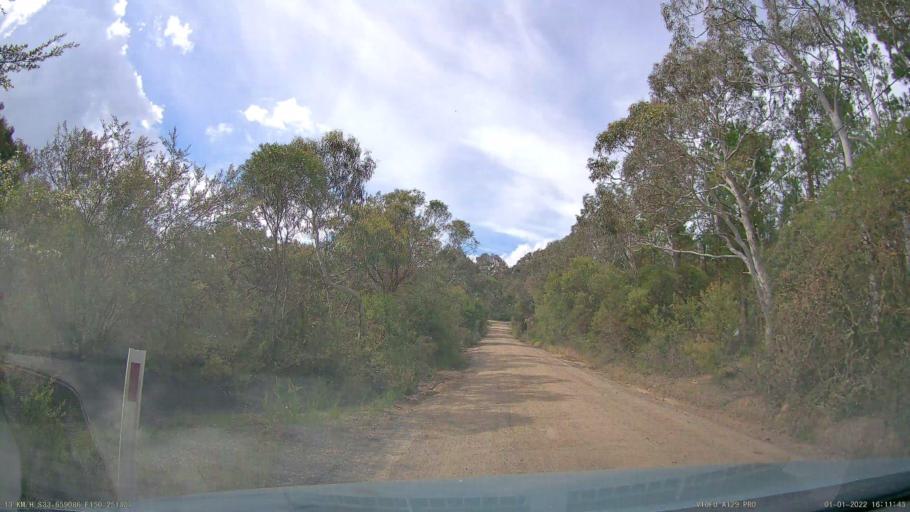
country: AU
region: New South Wales
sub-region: Blue Mountains Municipality
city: Blackheath
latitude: -33.6590
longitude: 150.2518
